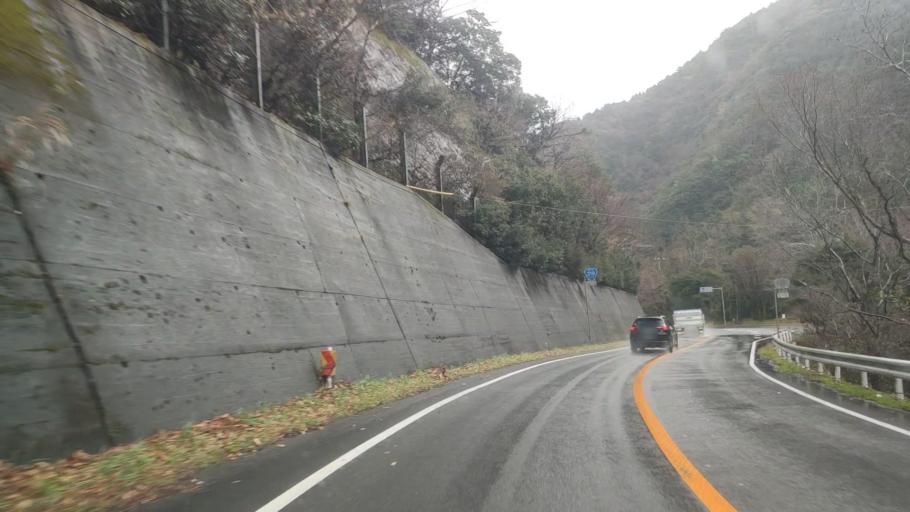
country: JP
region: Tokushima
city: Kamojimacho-jogejima
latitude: 34.1645
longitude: 134.3475
